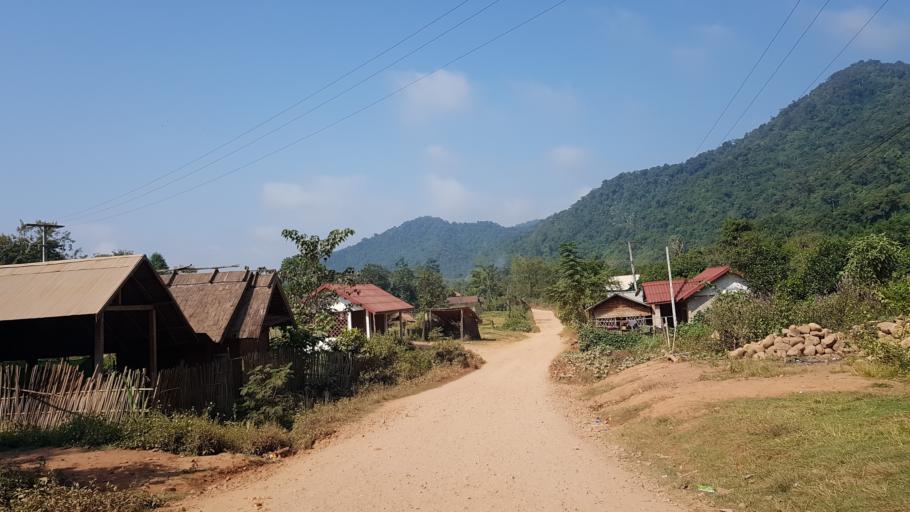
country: LA
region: Oudomxai
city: Muang Xay
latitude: 20.7213
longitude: 102.0521
